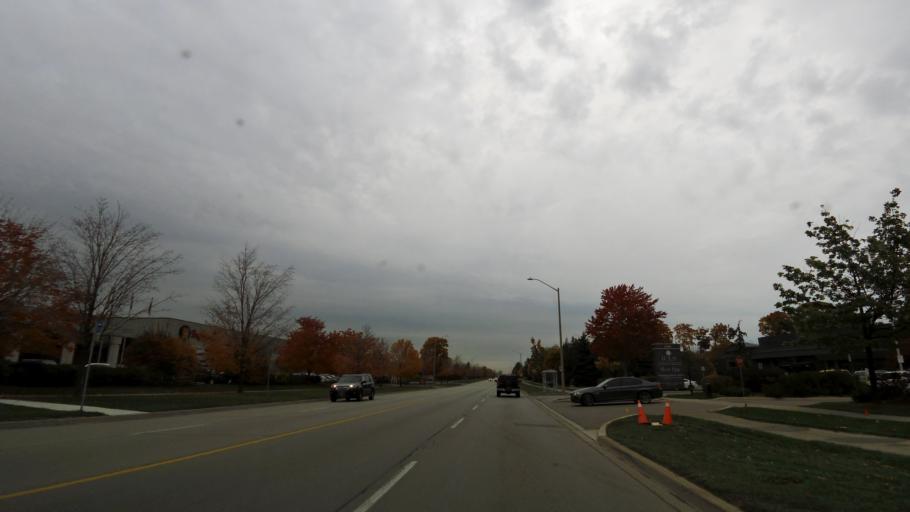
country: CA
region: Ontario
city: Oakville
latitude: 43.4732
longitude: -79.6643
